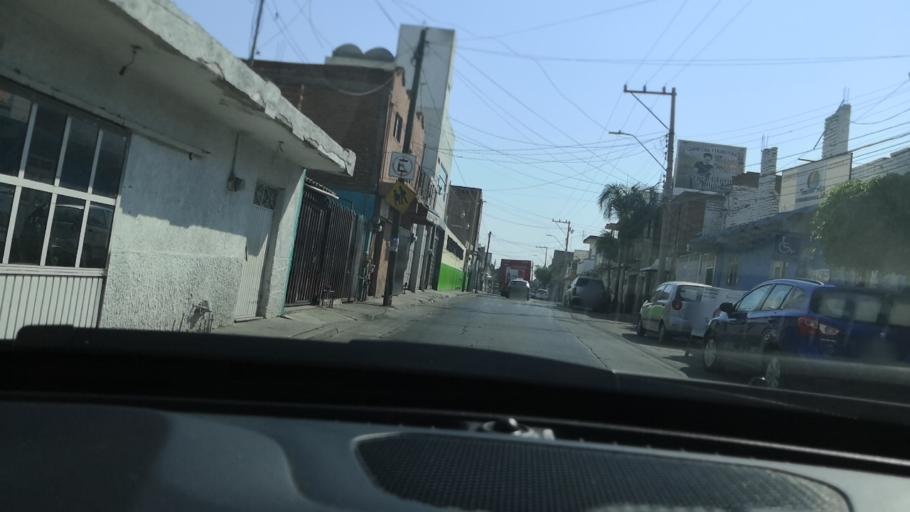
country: MX
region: Guanajuato
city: Leon
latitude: 21.1131
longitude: -101.6978
